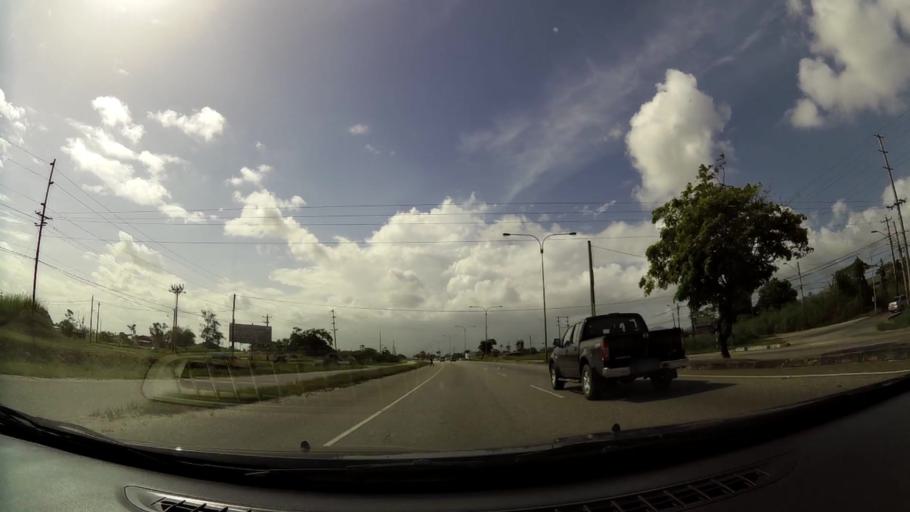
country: TT
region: Borough of Arima
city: Arima
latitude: 10.6131
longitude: -61.3009
